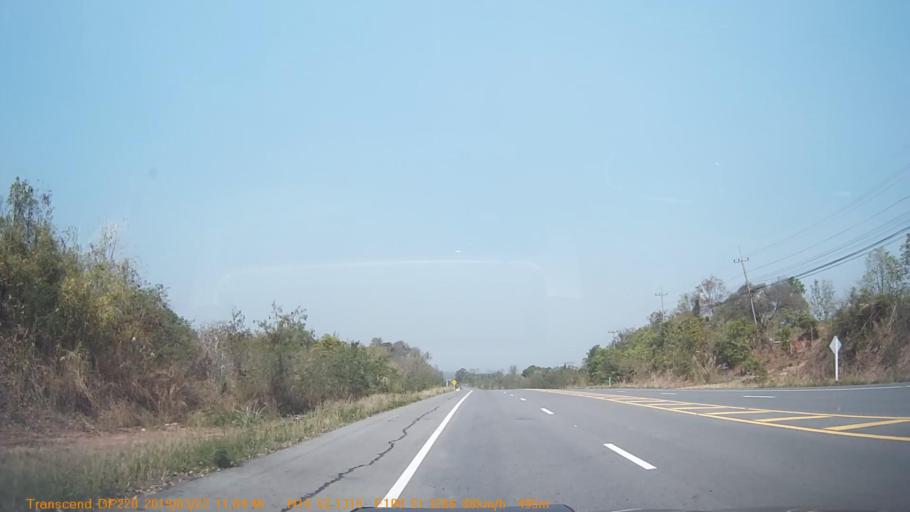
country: TH
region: Phitsanulok
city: Nakhon Thai
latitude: 16.8691
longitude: 100.8551
